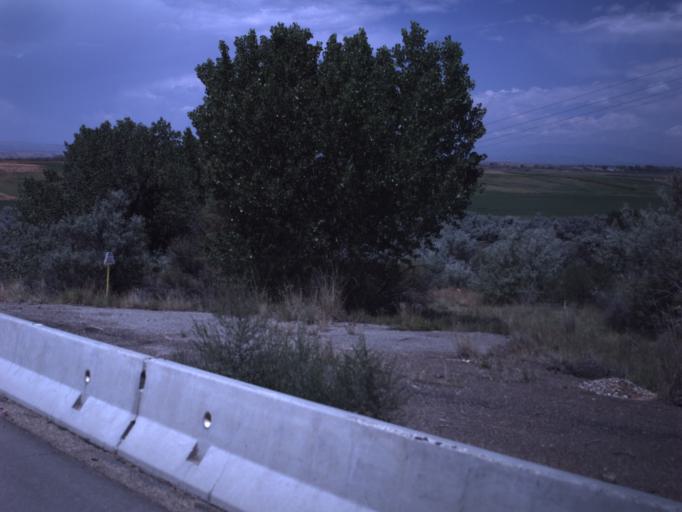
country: US
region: Utah
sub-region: Duchesne County
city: Roosevelt
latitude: 40.3020
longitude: -109.9052
